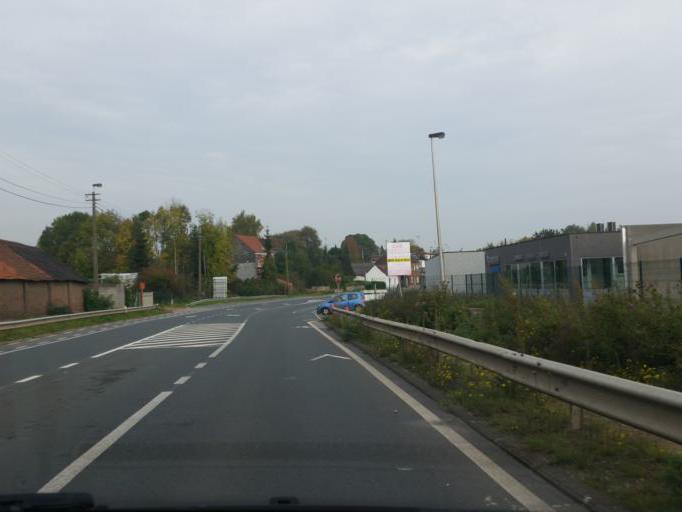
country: BE
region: Wallonia
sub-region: Province du Brabant Wallon
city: Tubize
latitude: 50.6996
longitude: 4.2054
